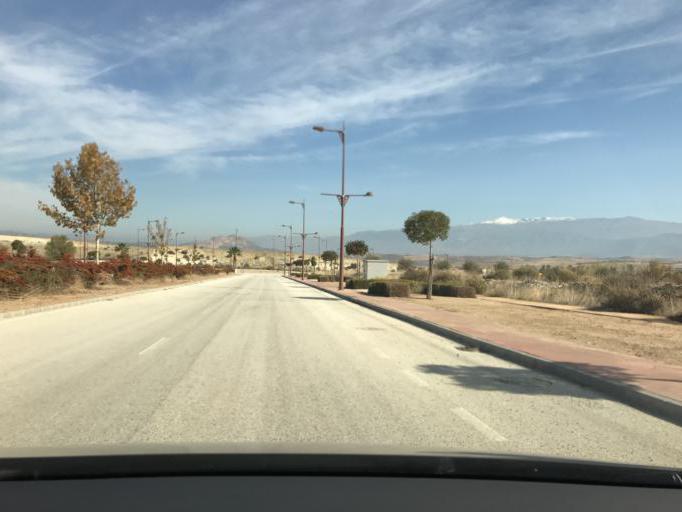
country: ES
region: Andalusia
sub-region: Provincia de Granada
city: Escuzar
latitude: 37.0840
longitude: -3.7504
